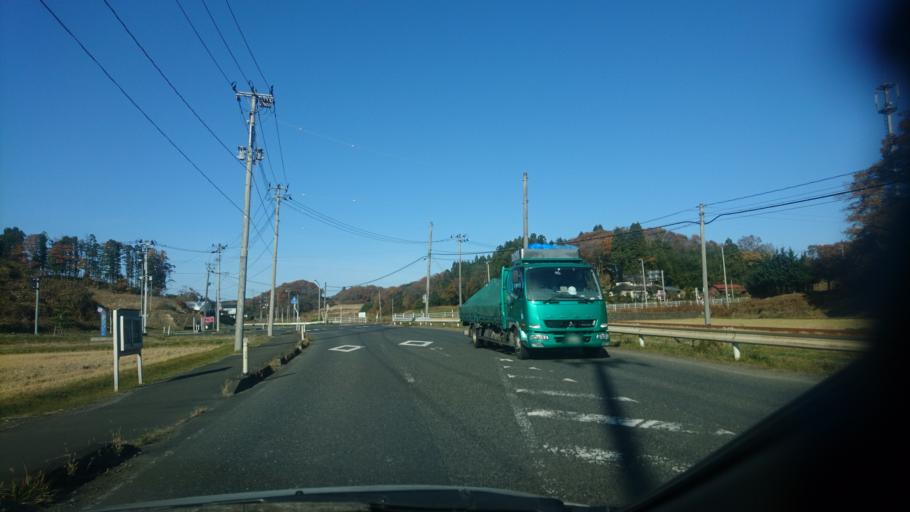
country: JP
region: Miyagi
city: Tomiya
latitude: 38.4609
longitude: 140.9048
